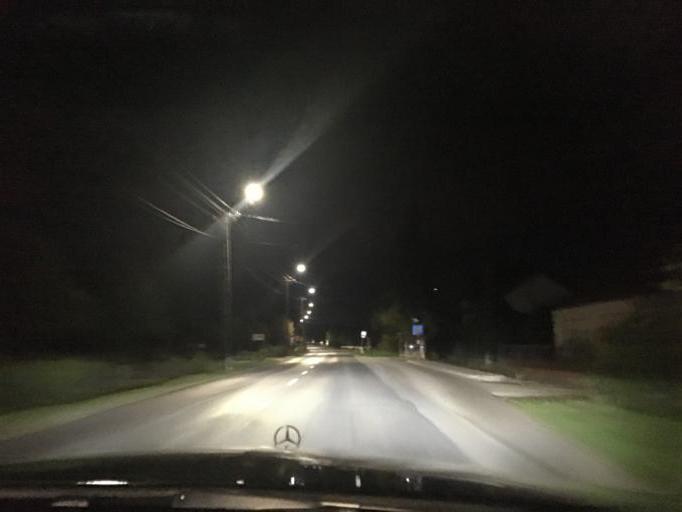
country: HU
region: Hajdu-Bihar
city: Hosszupalyi
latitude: 47.3974
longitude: 21.7279
